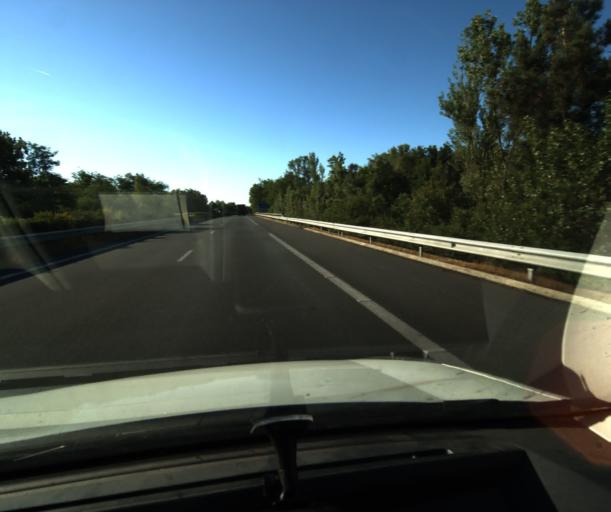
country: FR
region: Midi-Pyrenees
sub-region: Departement du Tarn-et-Garonne
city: Bressols
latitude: 43.9539
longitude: 1.2873
